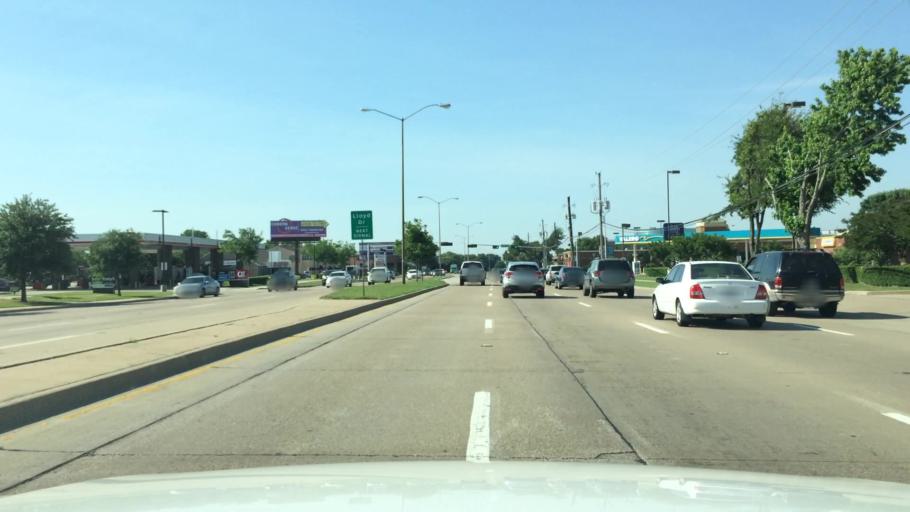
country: US
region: Texas
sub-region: Dallas County
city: Addison
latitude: 33.0090
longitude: -96.7955
